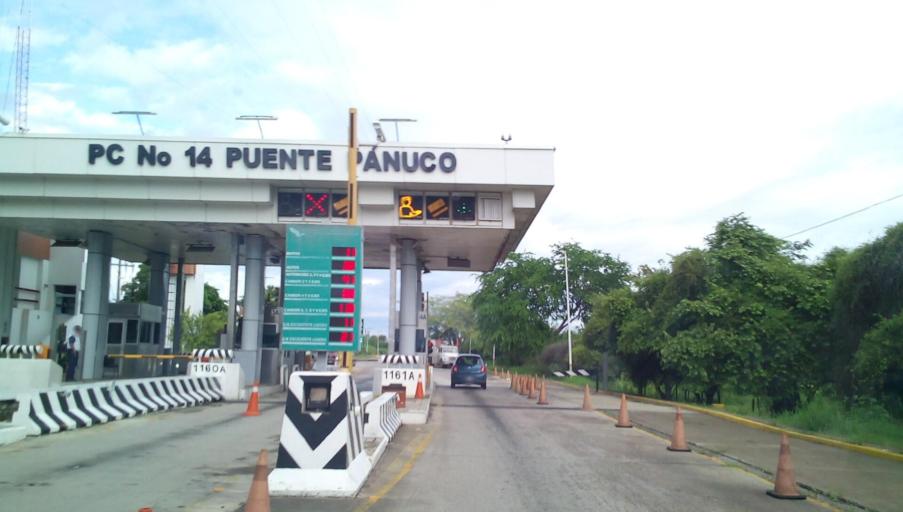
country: MX
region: Veracruz
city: Panuco
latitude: 22.1486
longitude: -98.1446
